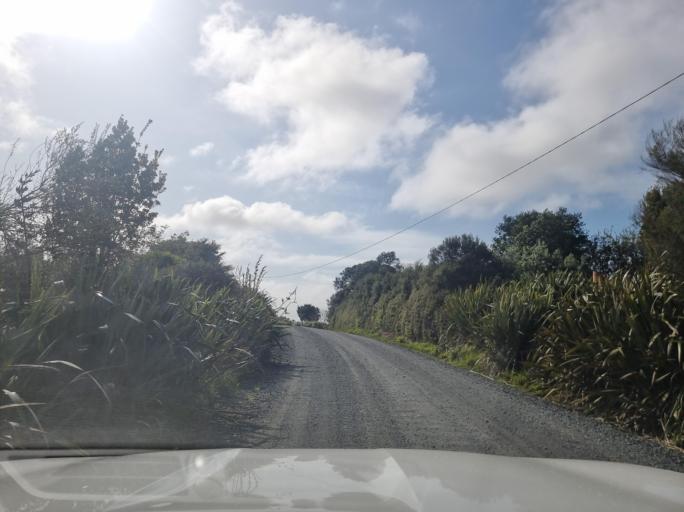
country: NZ
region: Northland
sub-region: Whangarei
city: Ruakaka
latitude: -36.0137
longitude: 174.4655
